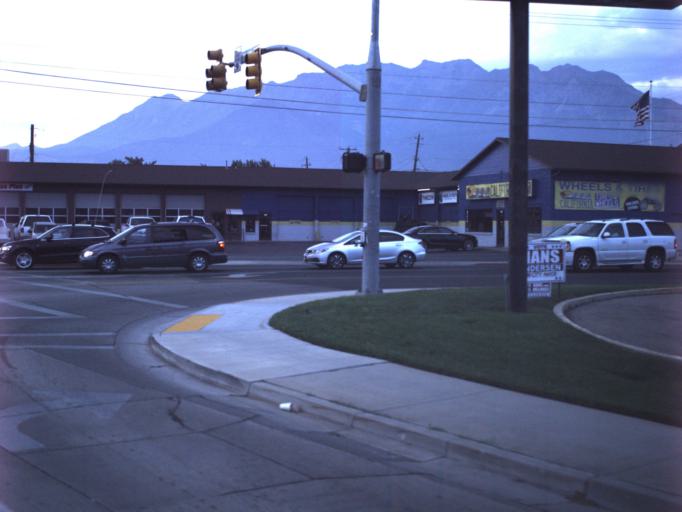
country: US
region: Utah
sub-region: Utah County
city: Orem
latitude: 40.2895
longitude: -111.6915
